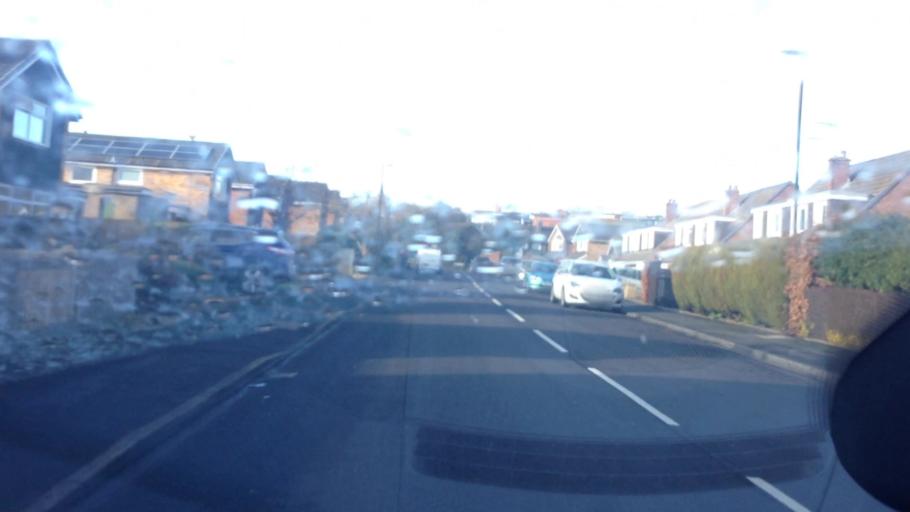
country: GB
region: England
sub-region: North Yorkshire
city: Knaresborough
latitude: 54.0023
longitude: -1.4550
